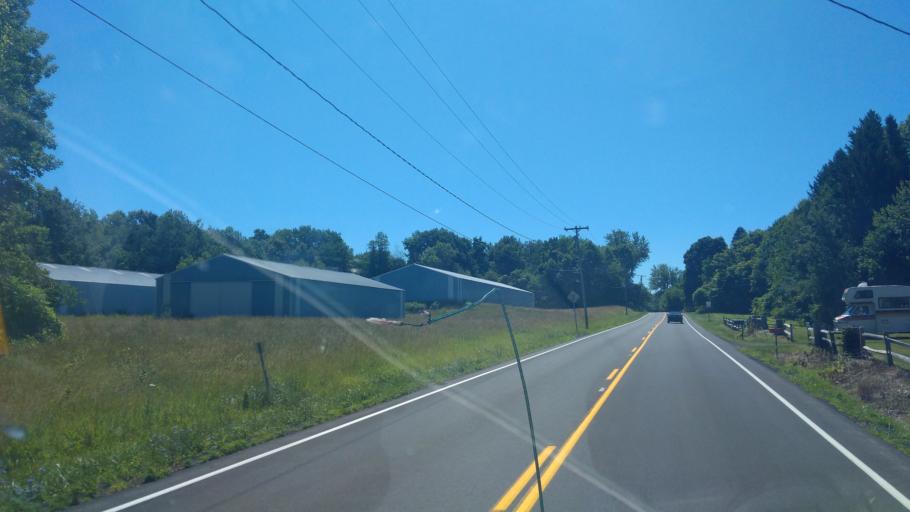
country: US
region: New York
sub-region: Wayne County
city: Sodus
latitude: 43.2454
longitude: -76.9886
